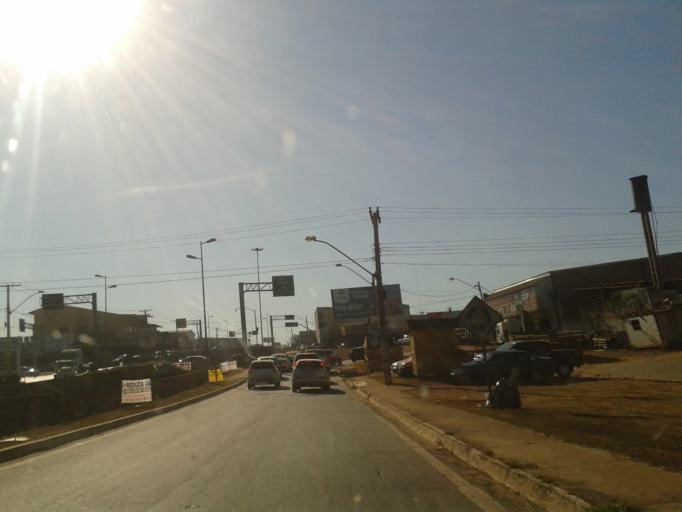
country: BR
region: Goias
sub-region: Goiania
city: Goiania
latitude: -16.6930
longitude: -49.3203
